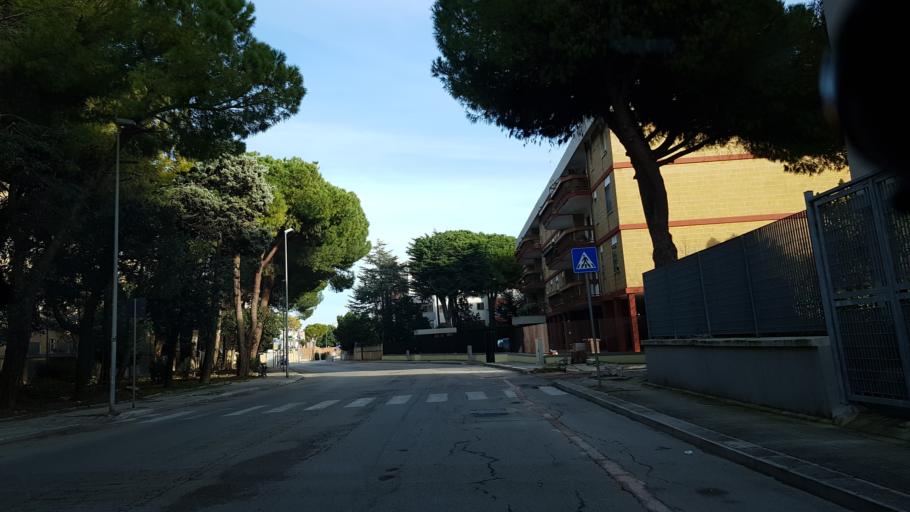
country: IT
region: Apulia
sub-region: Provincia di Brindisi
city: Brindisi
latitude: 40.6191
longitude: 17.9225
